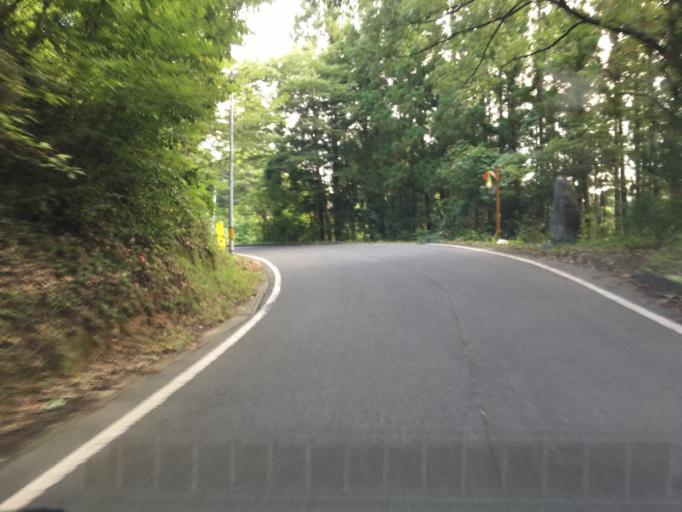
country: JP
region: Fukushima
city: Fukushima-shi
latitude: 37.6878
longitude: 140.5736
